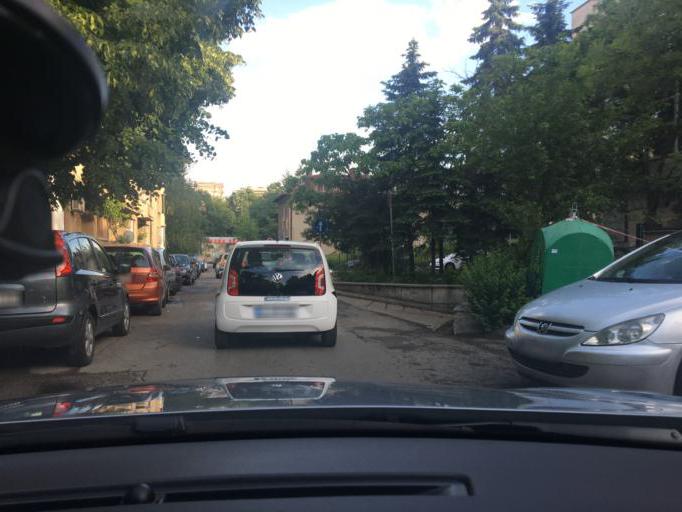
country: BG
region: Sofia-Capital
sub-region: Stolichna Obshtina
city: Sofia
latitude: 42.6742
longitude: 23.3495
